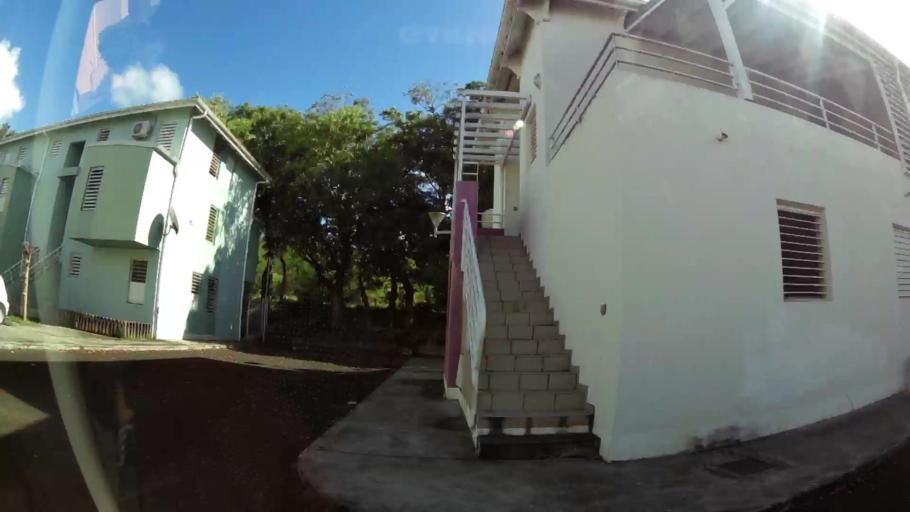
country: GP
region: Guadeloupe
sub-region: Guadeloupe
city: Port-Louis
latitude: 16.4130
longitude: -61.5259
